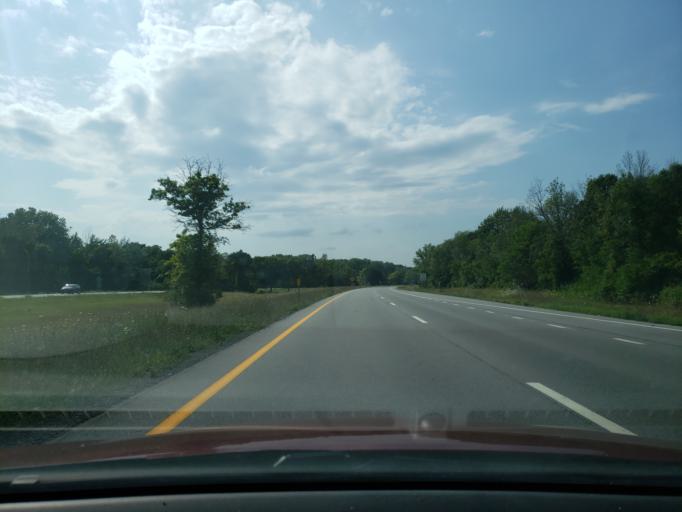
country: US
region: New York
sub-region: Monroe County
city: Irondequoit
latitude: 43.2564
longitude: -77.6325
